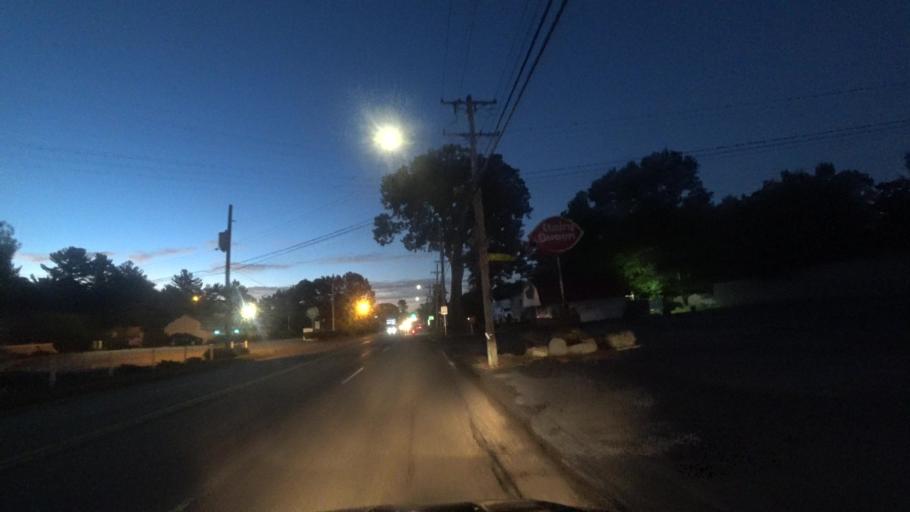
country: US
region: Massachusetts
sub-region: Middlesex County
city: North Reading
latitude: 42.5944
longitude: -71.1192
